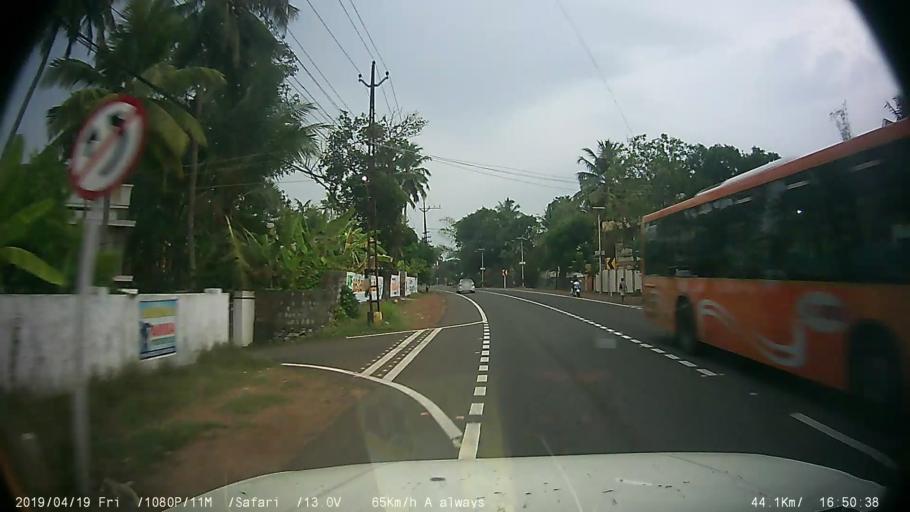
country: IN
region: Kerala
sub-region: Kottayam
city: Changanacheri
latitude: 9.4625
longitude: 76.5318
